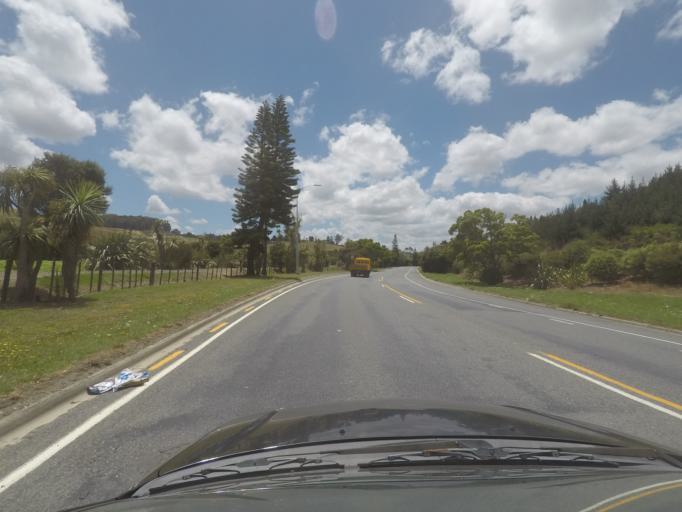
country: NZ
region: Northland
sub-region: Whangarei
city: Whangarei
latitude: -35.7492
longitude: 174.3204
